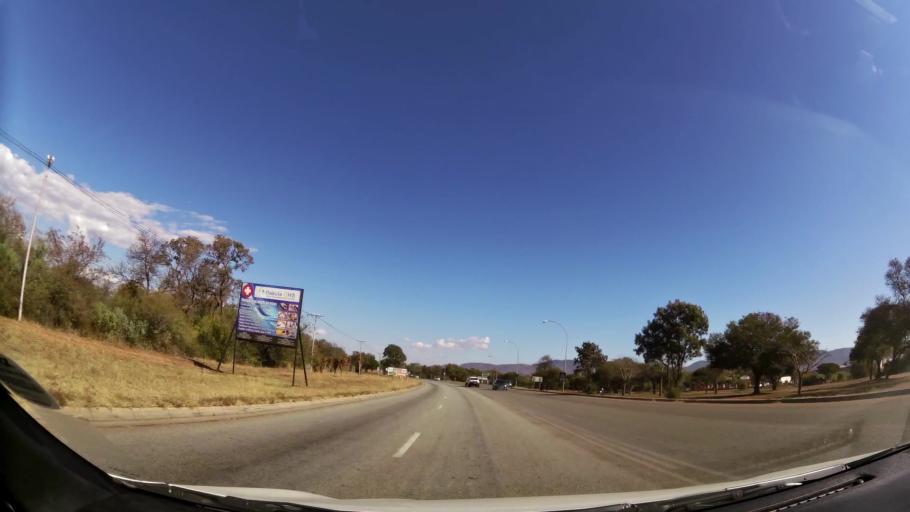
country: ZA
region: Limpopo
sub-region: Waterberg District Municipality
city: Mokopane
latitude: -24.1683
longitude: 29.0187
